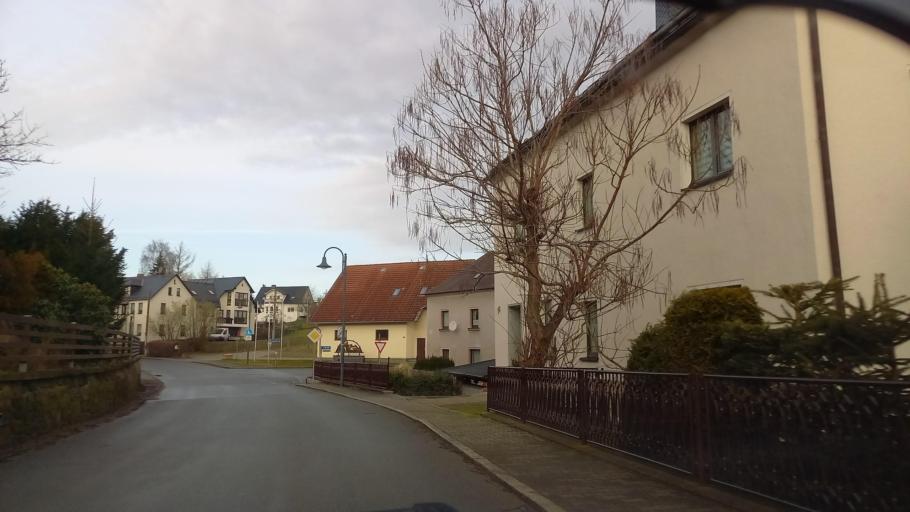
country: DE
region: Saxony
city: Hirschfeld
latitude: 50.6252
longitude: 12.4602
